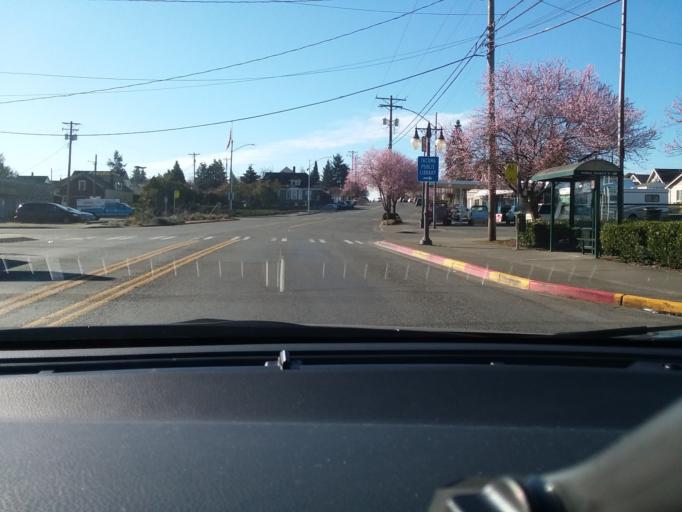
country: US
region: Washington
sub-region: Pierce County
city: Tacoma
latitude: 47.2289
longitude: -122.4207
